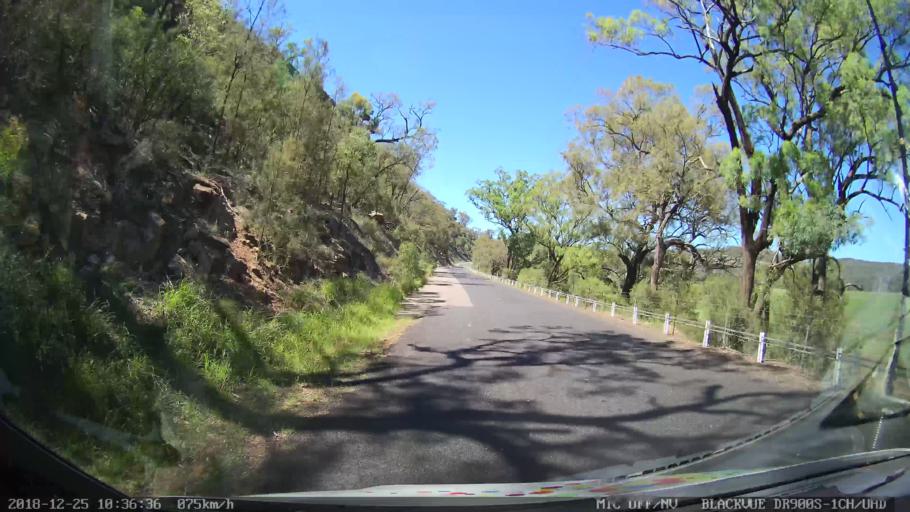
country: AU
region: New South Wales
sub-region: Upper Hunter Shire
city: Merriwa
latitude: -32.4054
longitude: 150.3842
